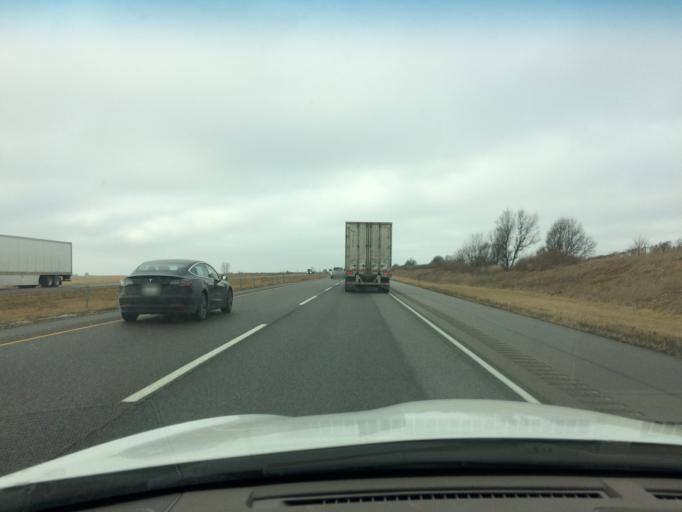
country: US
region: Illinois
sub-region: Kane County
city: Maple Park
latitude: 41.8708
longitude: -88.5894
